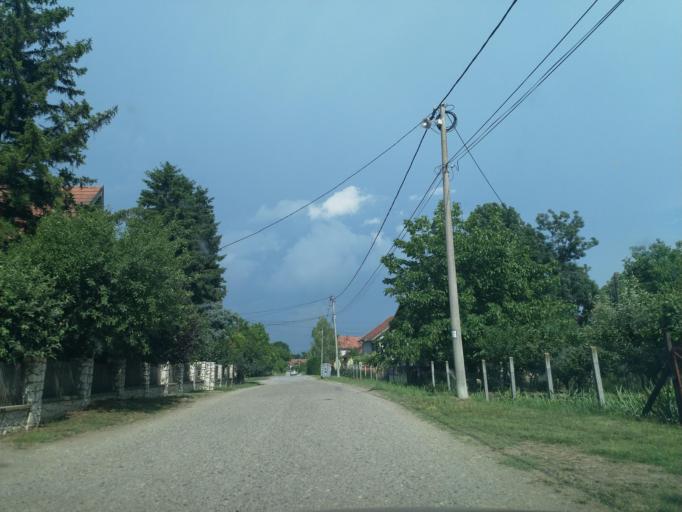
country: RS
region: Central Serbia
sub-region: Pomoravski Okrug
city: Cuprija
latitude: 43.9547
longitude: 21.3221
